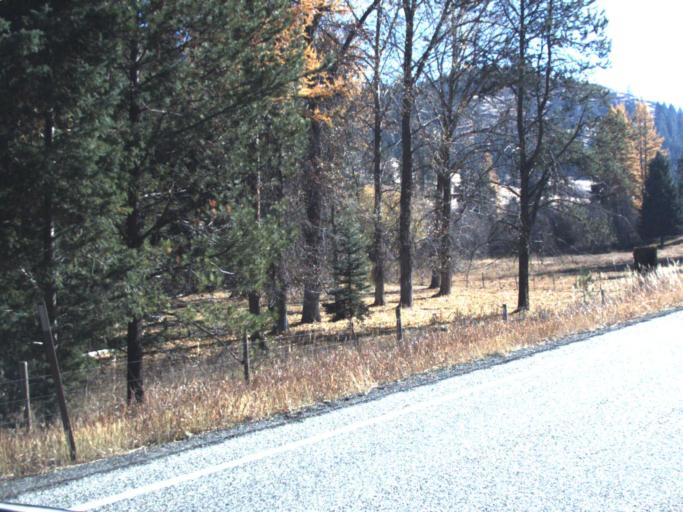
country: US
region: Washington
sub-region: Ferry County
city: Republic
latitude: 48.6117
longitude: -118.6628
